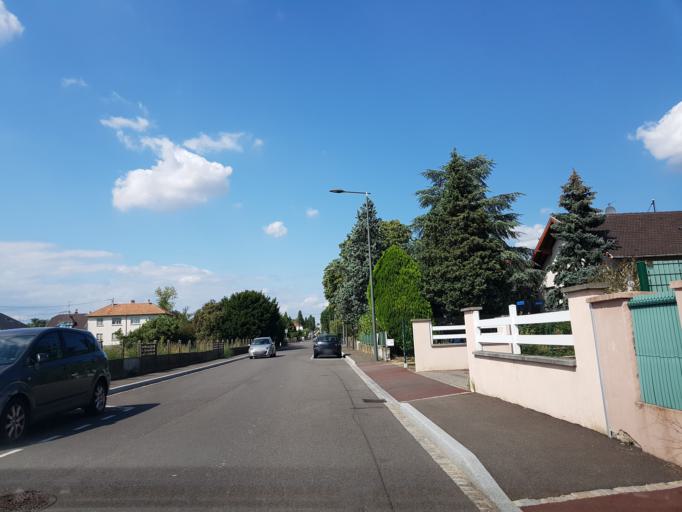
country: FR
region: Alsace
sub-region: Departement du Haut-Rhin
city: Illzach
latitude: 47.7792
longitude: 7.3528
